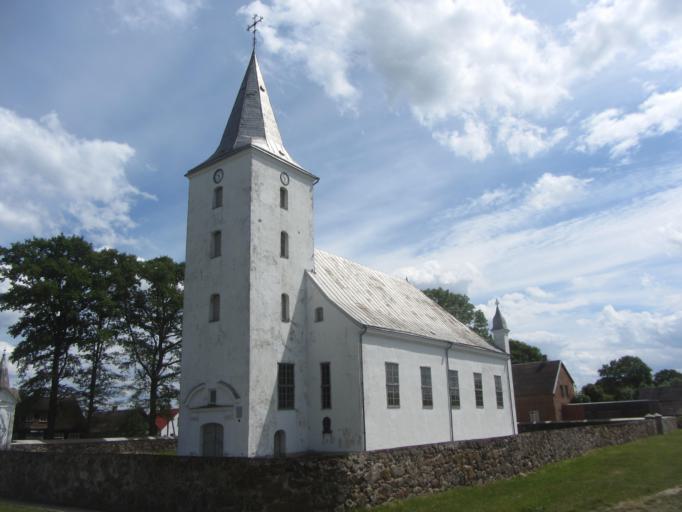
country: LT
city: Obeliai
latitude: 56.1189
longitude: 25.0032
